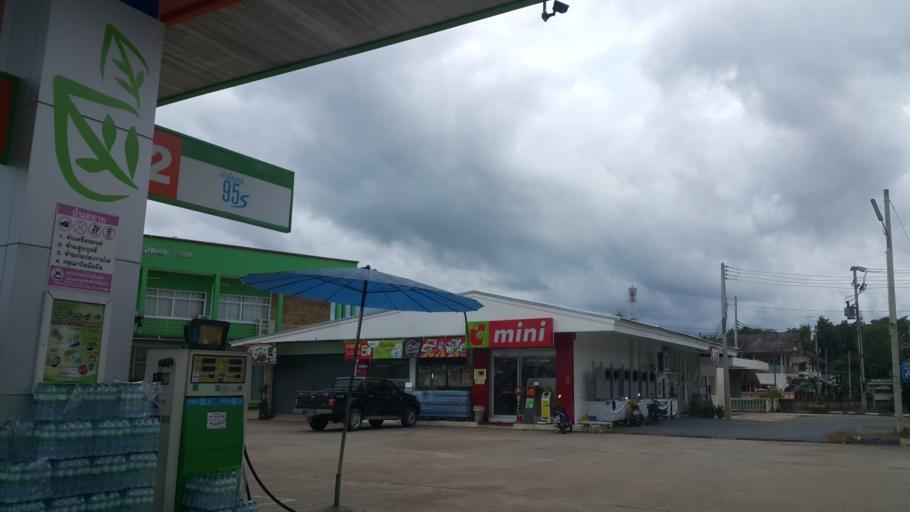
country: TH
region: Sukhothai
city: Thung Saliam
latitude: 17.3220
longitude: 99.5655
